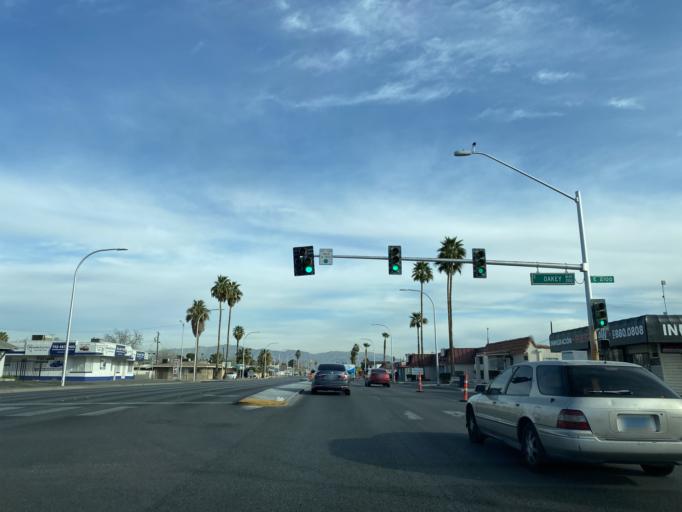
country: US
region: Nevada
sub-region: Clark County
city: Winchester
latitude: 36.1516
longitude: -115.1188
